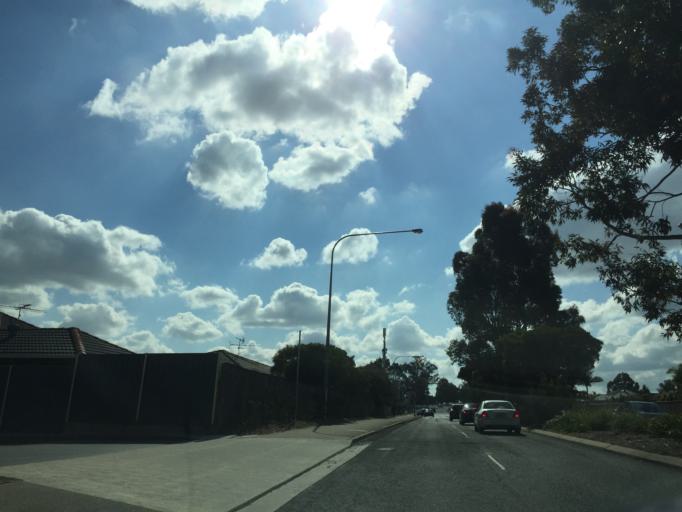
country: AU
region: New South Wales
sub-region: Blacktown
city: Quakers Hill
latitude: -33.7195
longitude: 150.8923
